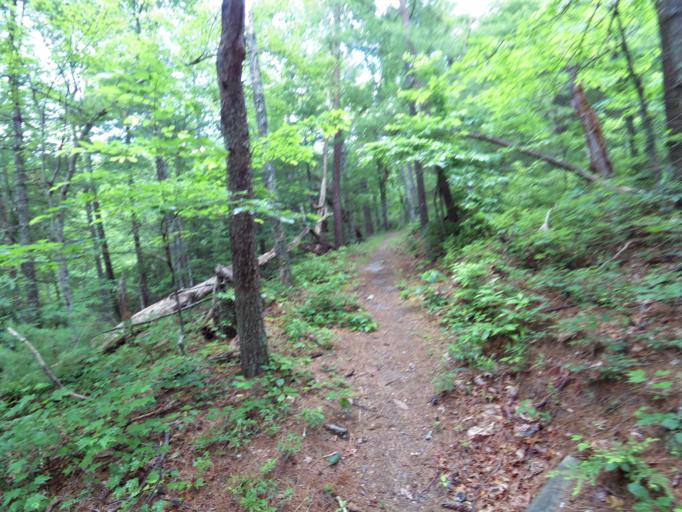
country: US
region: Tennessee
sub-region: Blount County
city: Wildwood
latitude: 35.6608
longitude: -83.8272
